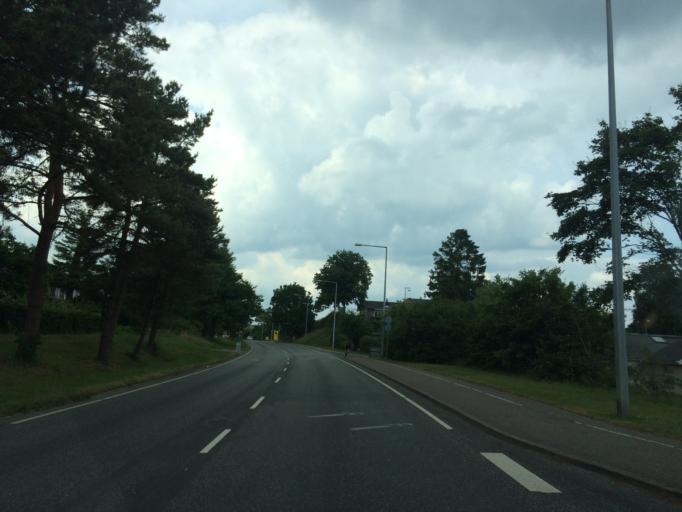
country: DK
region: South Denmark
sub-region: Middelfart Kommune
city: Strib
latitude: 55.5292
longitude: 9.7711
